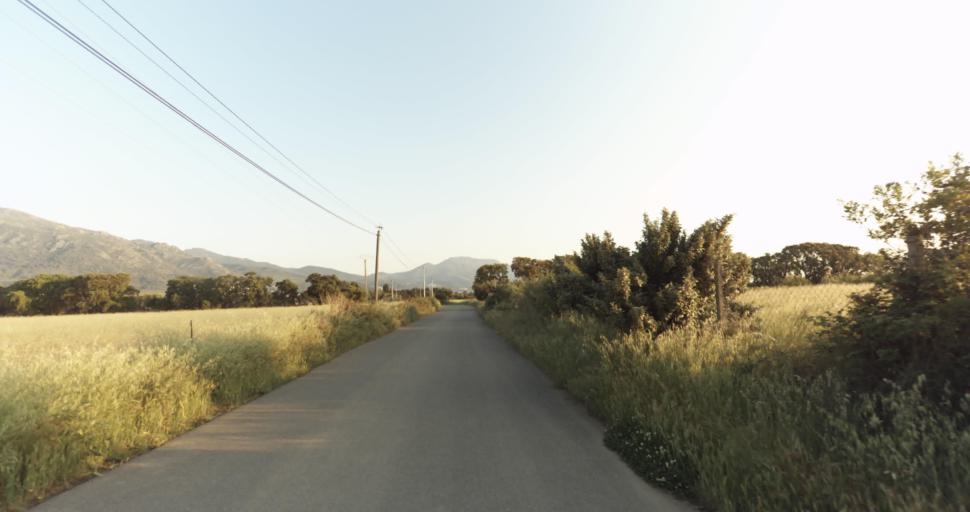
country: FR
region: Corsica
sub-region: Departement de la Haute-Corse
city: Biguglia
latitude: 42.6087
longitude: 9.4492
